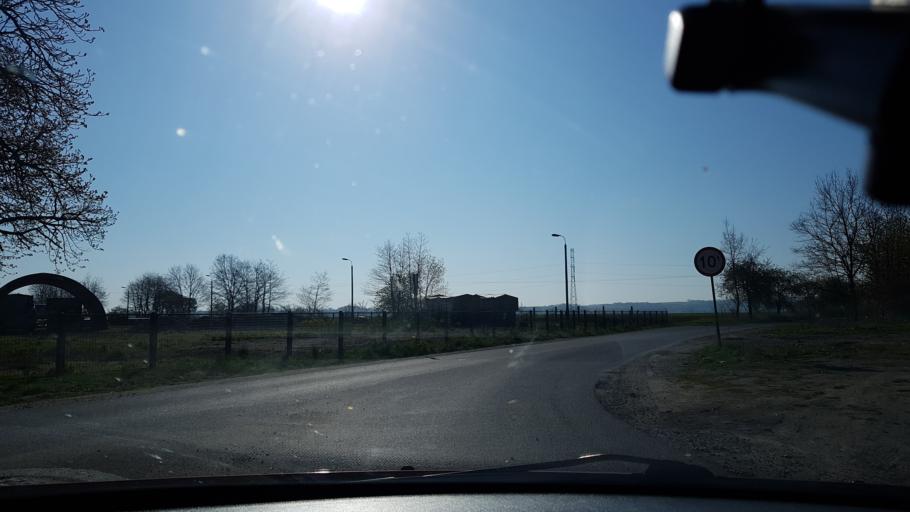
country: PL
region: Opole Voivodeship
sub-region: Powiat nyski
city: Nysa
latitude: 50.4294
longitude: 17.3058
